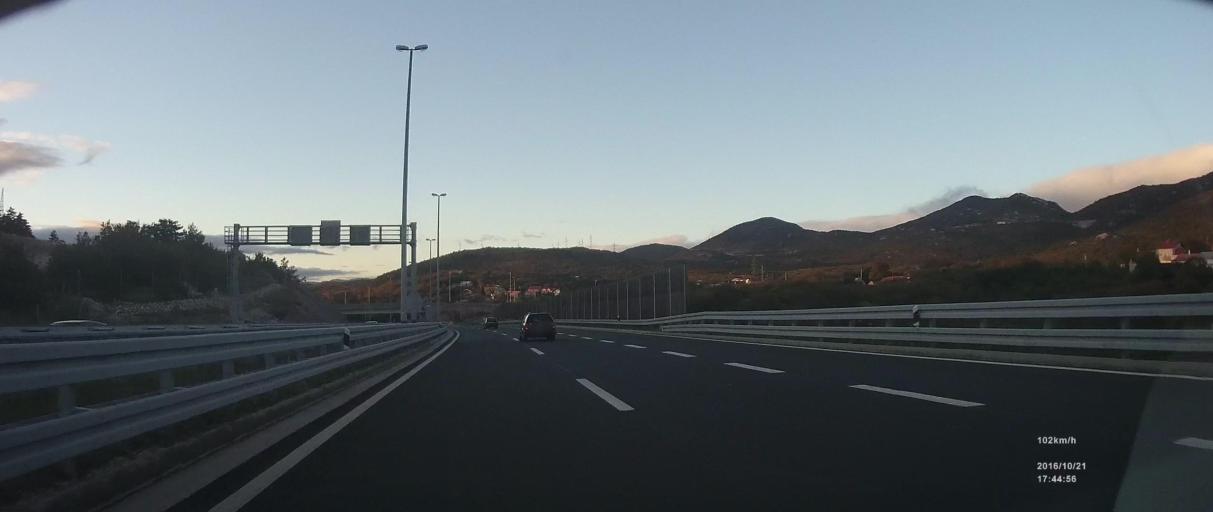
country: HR
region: Primorsko-Goranska
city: Hreljin
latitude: 45.2861
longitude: 14.5873
